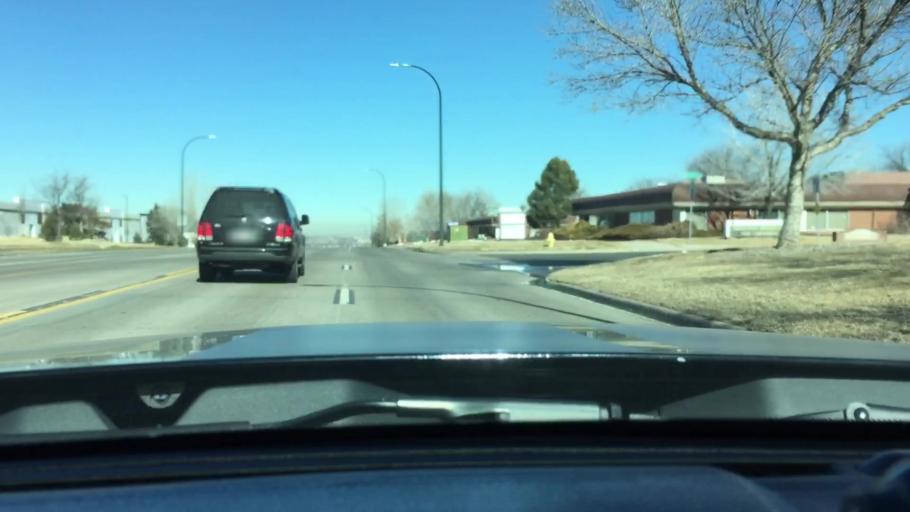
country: US
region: Colorado
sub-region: Adams County
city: Northglenn
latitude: 39.9078
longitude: -104.9966
